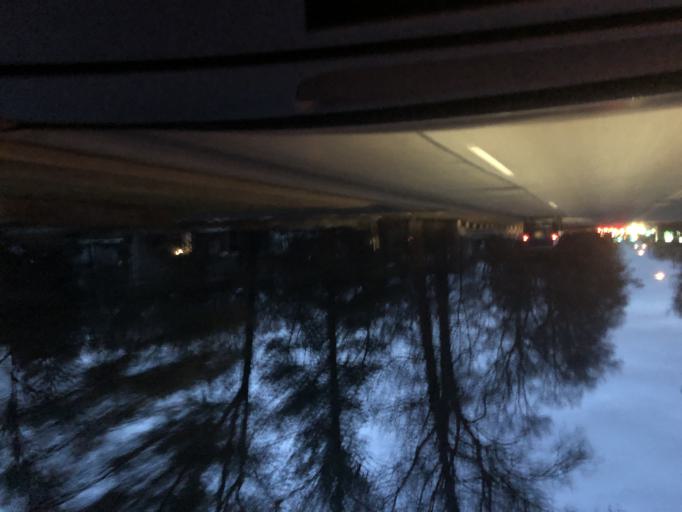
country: US
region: New Jersey
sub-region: Morris County
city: Florham Park
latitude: 40.7845
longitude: -74.3826
